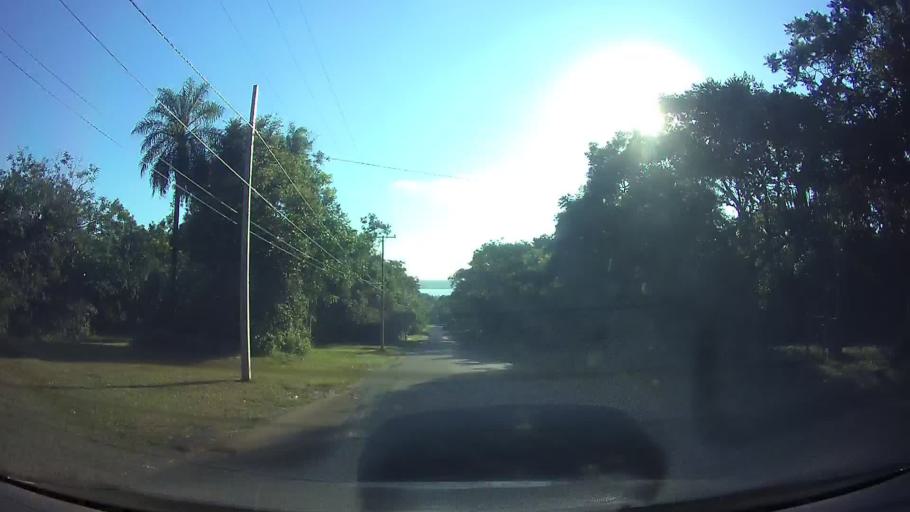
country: PY
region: Cordillera
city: San Bernardino
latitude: -25.3177
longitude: -57.2691
